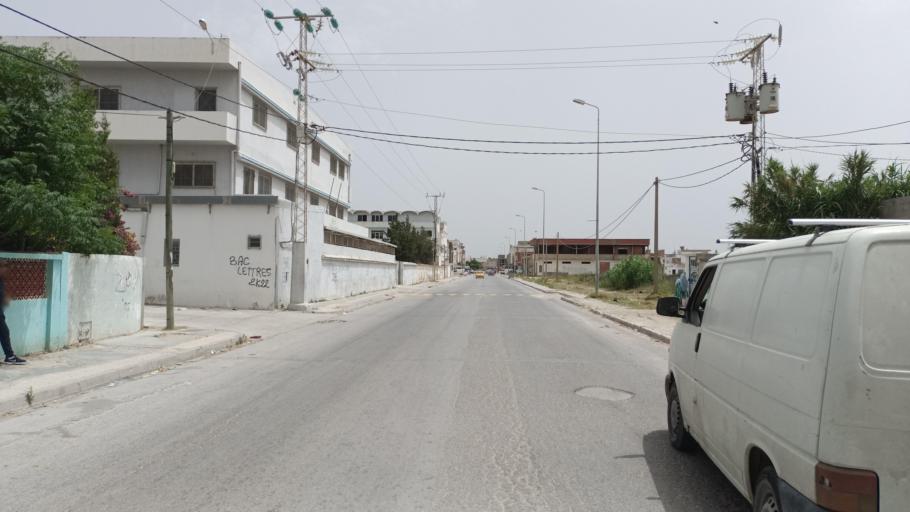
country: TN
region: Nabul
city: Manzil Bu Zalafah
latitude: 36.7070
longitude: 10.4850
